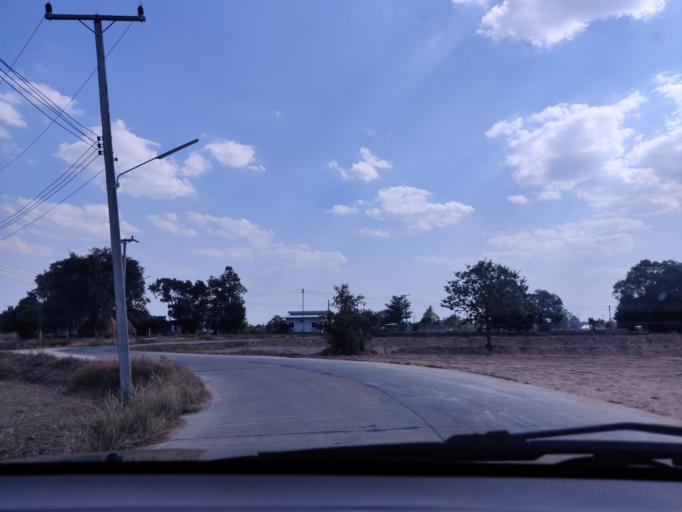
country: TH
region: Sisaket
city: Si Sa Ket
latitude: 15.0875
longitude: 104.3531
